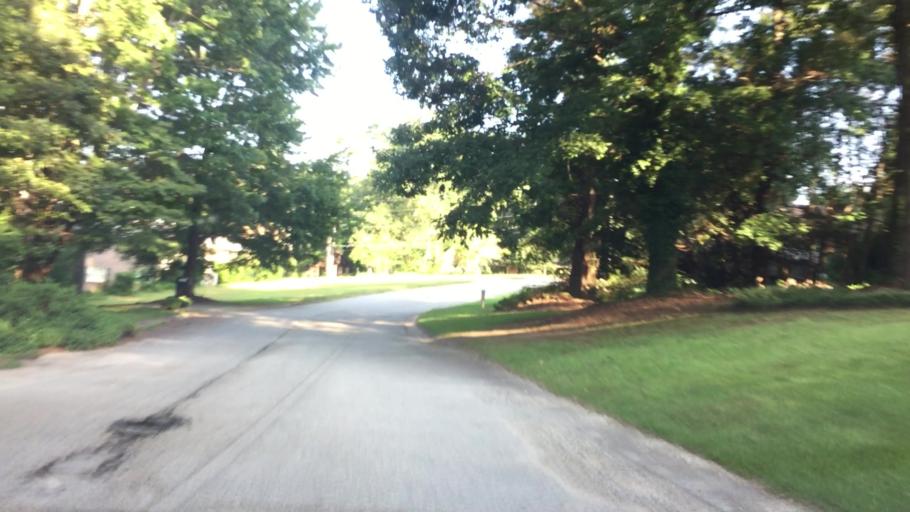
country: US
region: Georgia
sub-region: Henry County
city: Stockbridge
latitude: 33.6205
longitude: -84.2278
